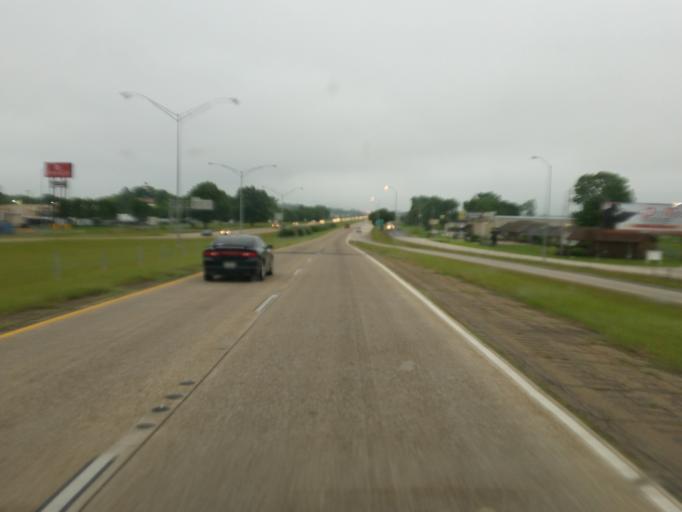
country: US
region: Louisiana
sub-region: Bossier Parish
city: Bossier City
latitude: 32.5289
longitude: -93.6724
